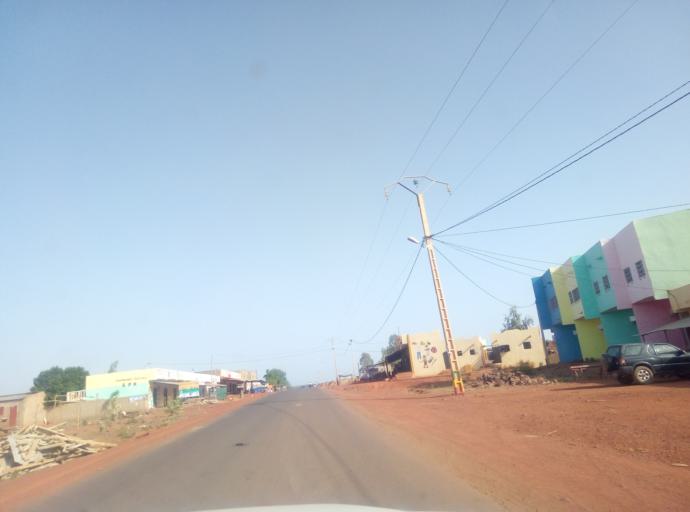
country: ML
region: Bamako
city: Bamako
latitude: 12.6010
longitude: -7.7694
